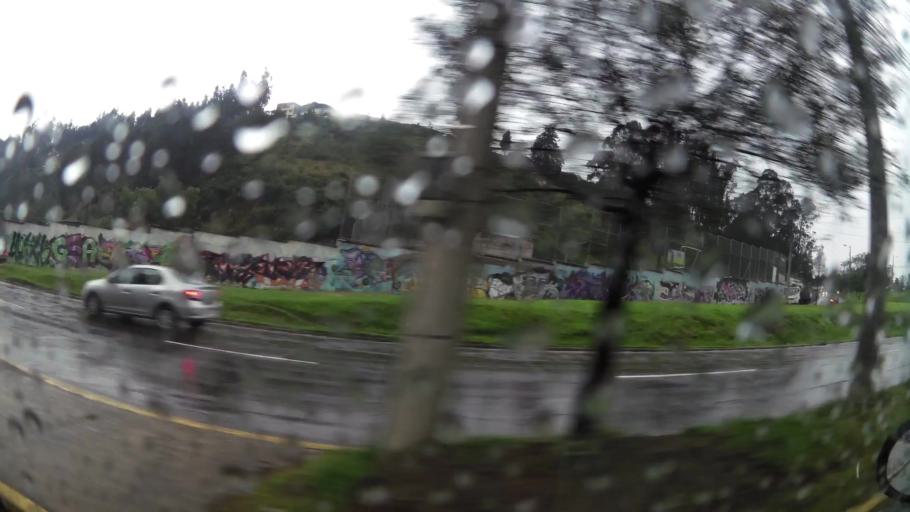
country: EC
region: Pichincha
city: Quito
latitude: -0.1519
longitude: -78.4636
